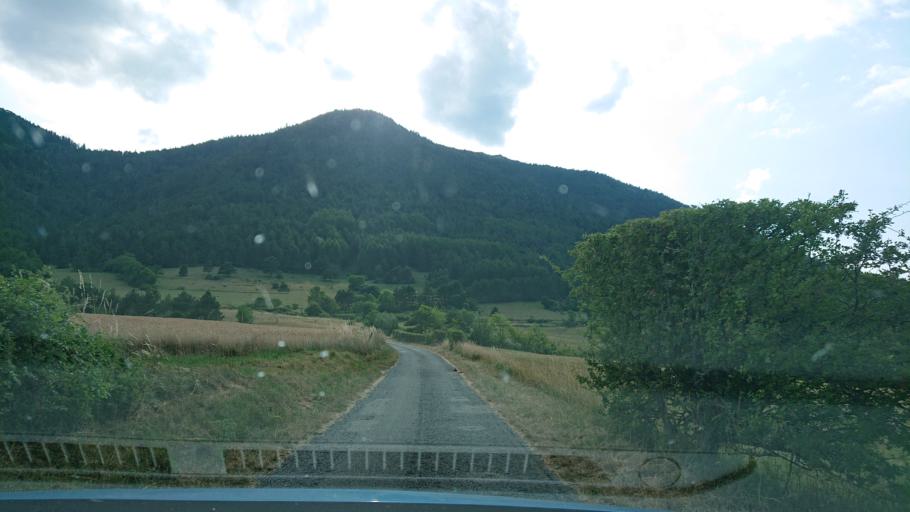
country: FR
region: Rhone-Alpes
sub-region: Departement de l'Isere
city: Mens
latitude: 44.7968
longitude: 5.9009
